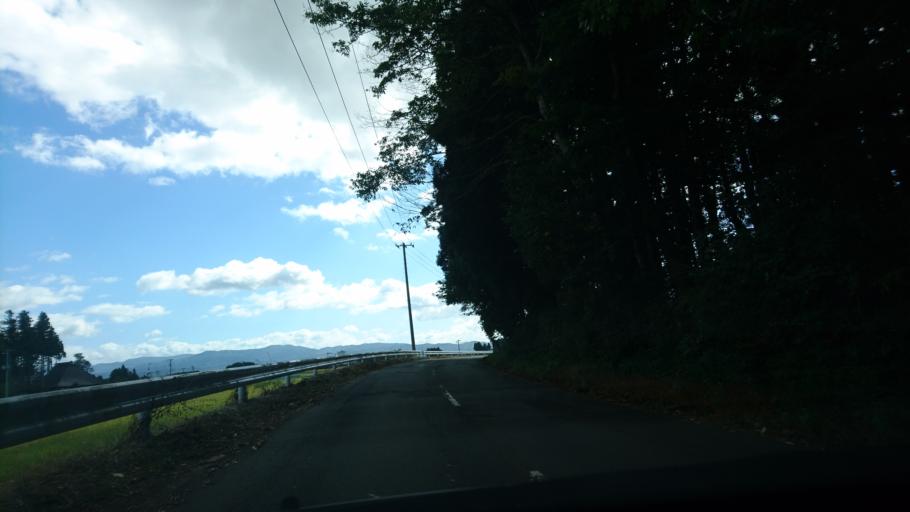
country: JP
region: Iwate
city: Mizusawa
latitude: 39.0806
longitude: 141.1022
